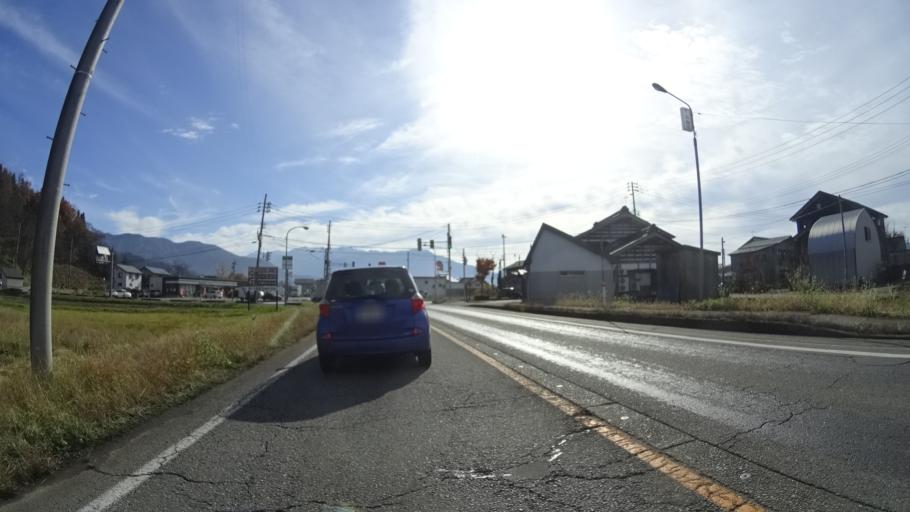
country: JP
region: Niigata
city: Muikamachi
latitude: 37.1157
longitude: 138.9204
